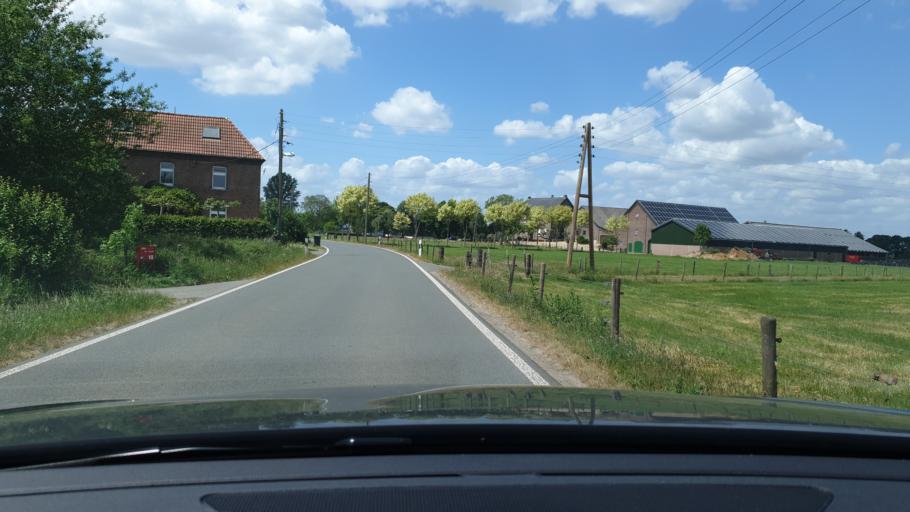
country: DE
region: North Rhine-Westphalia
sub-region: Regierungsbezirk Dusseldorf
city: Kranenburg
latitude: 51.8121
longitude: 6.0473
